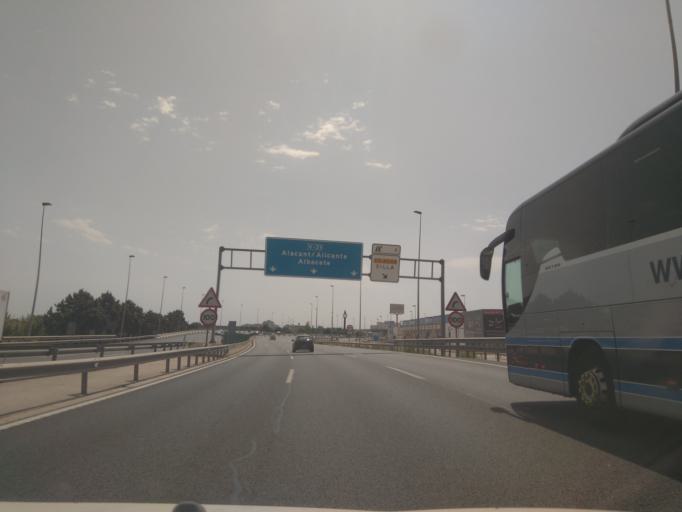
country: ES
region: Valencia
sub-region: Provincia de Valencia
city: Beniparrell
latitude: 39.3817
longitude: -0.3995
